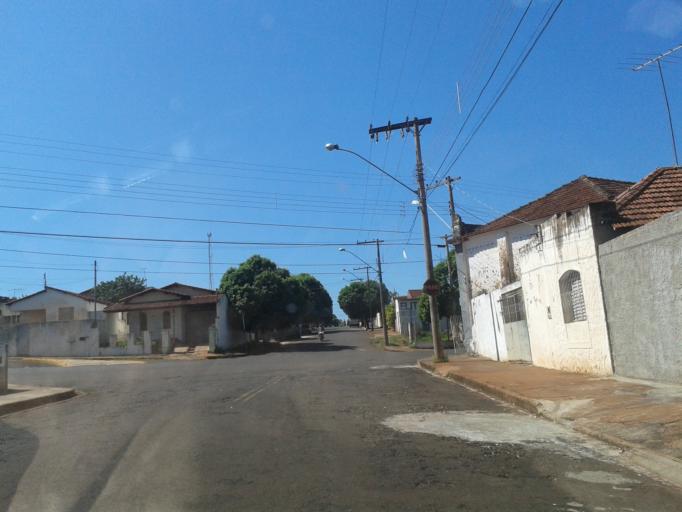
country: BR
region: Minas Gerais
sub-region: Ituiutaba
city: Ituiutaba
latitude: -18.9812
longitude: -49.4715
